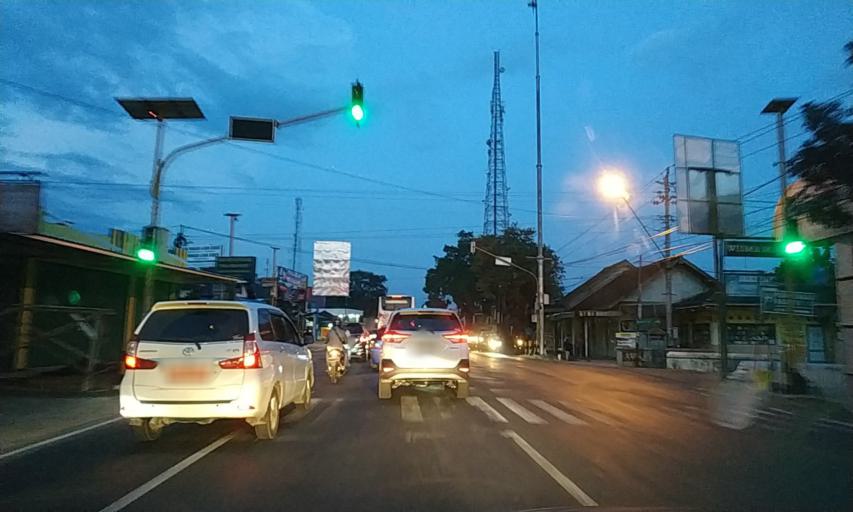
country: ID
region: Daerah Istimewa Yogyakarta
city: Godean
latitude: -7.8143
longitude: 110.2566
